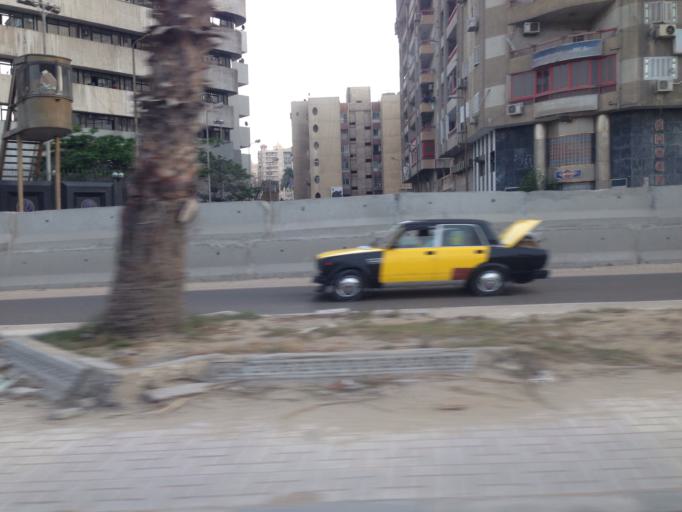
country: EG
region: Alexandria
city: Alexandria
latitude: 31.2127
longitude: 29.9522
